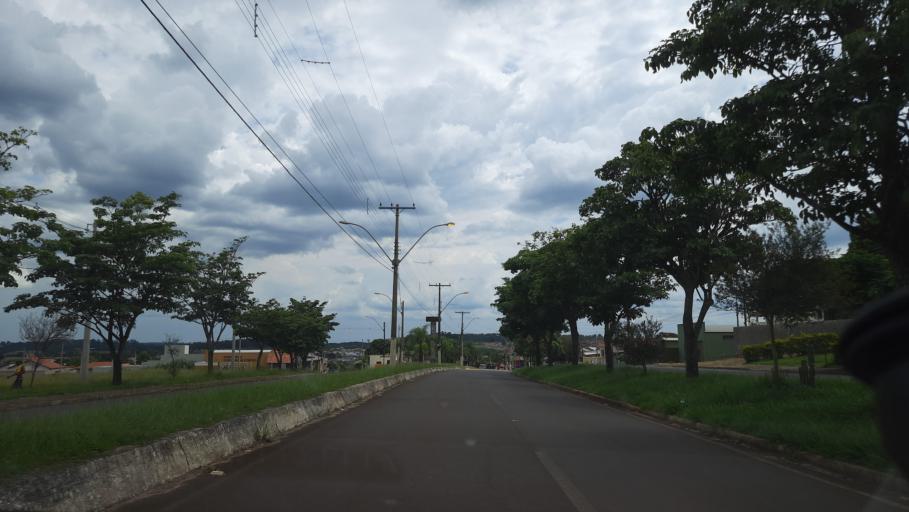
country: BR
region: Sao Paulo
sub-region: Cajuru
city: Cajuru
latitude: -21.2750
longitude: -47.2938
